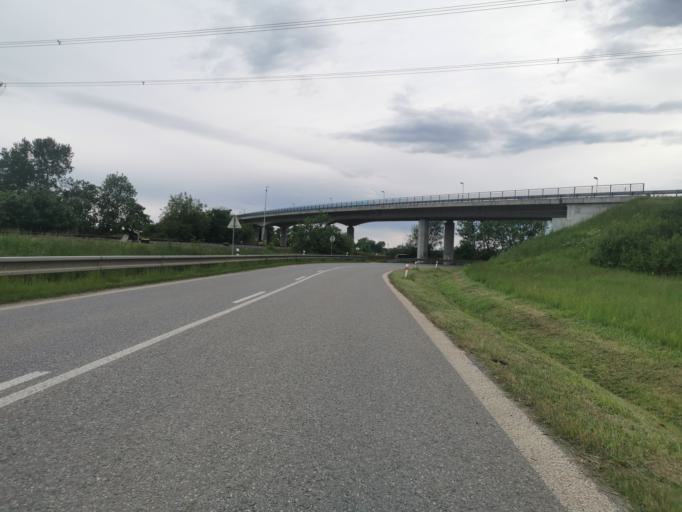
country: CZ
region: South Moravian
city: Sudomerice
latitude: 48.8706
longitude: 17.2412
